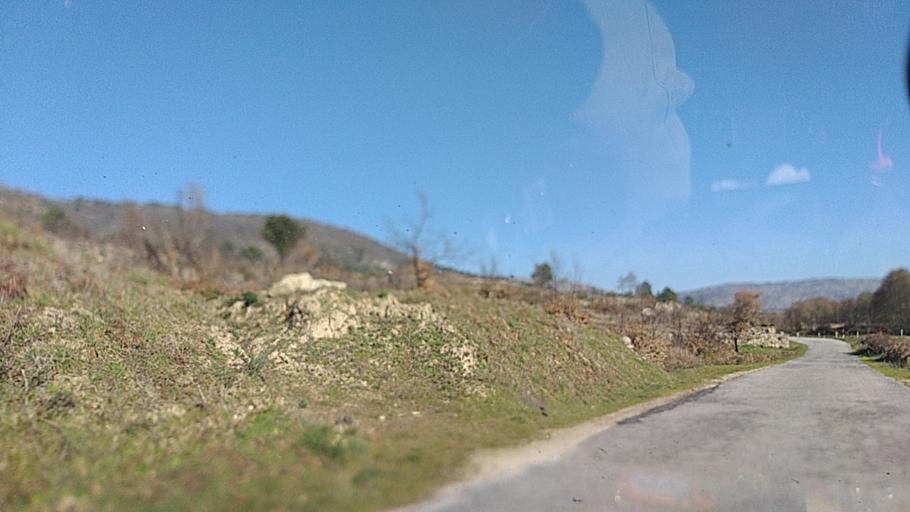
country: PT
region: Guarda
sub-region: Celorico da Beira
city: Celorico da Beira
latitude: 40.6767
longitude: -7.4558
